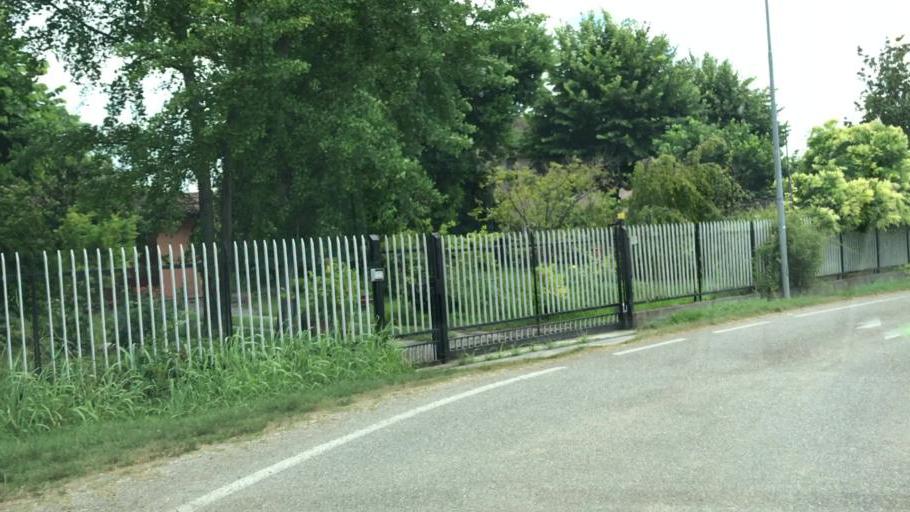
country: IT
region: Lombardy
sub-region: Provincia di Mantova
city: Ceresara
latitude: 45.2674
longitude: 10.5757
